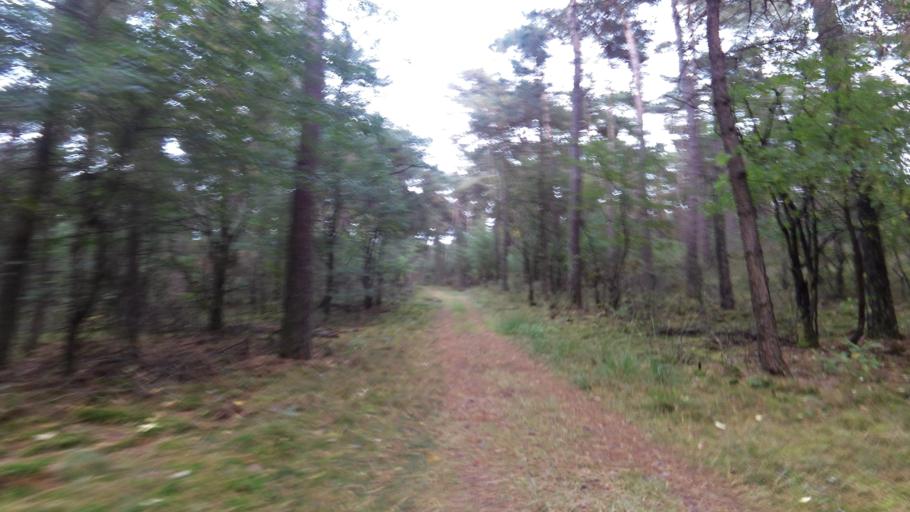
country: NL
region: Gelderland
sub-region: Gemeente Ede
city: Harskamp
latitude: 52.1565
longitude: 5.7499
